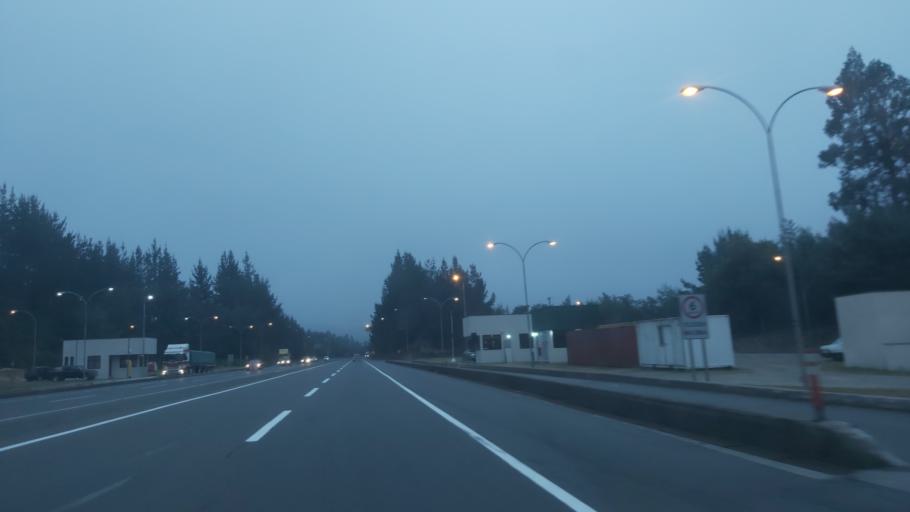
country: CL
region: Biobio
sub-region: Provincia de Concepcion
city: Penco
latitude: -36.7353
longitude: -72.8878
